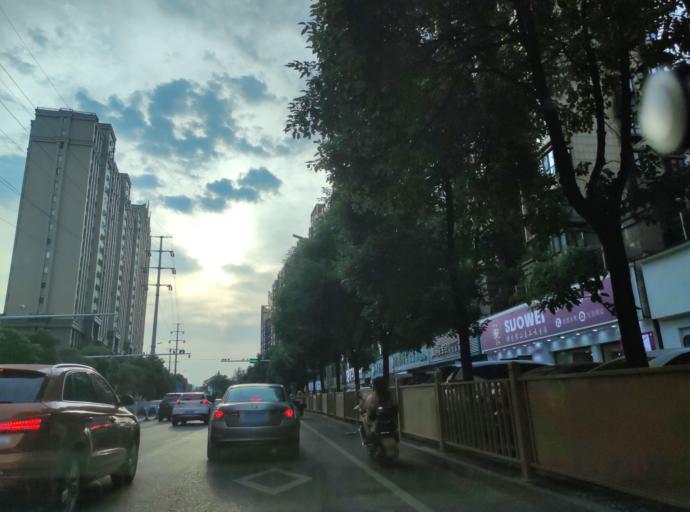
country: CN
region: Jiangxi Sheng
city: Pingxiang
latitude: 27.6336
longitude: 113.8671
